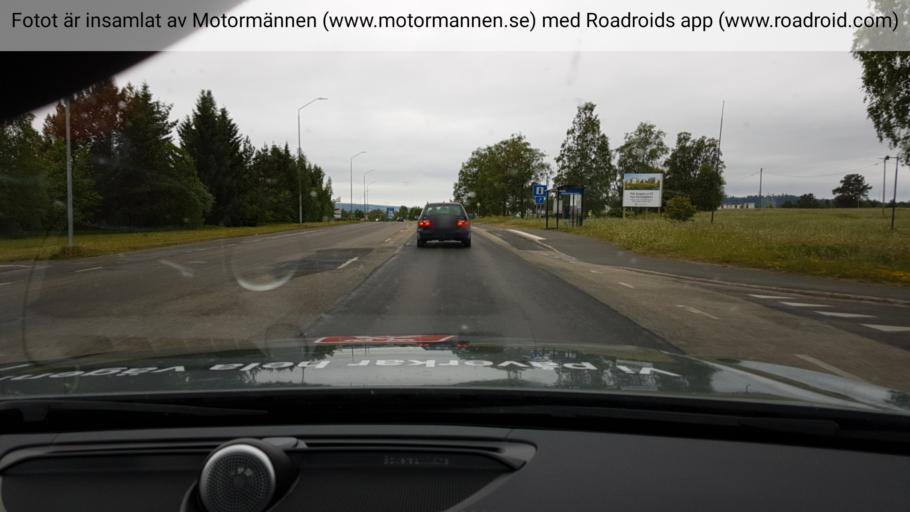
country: SE
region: Jaemtland
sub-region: OEstersunds Kommun
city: Ostersund
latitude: 63.1780
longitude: 14.6721
